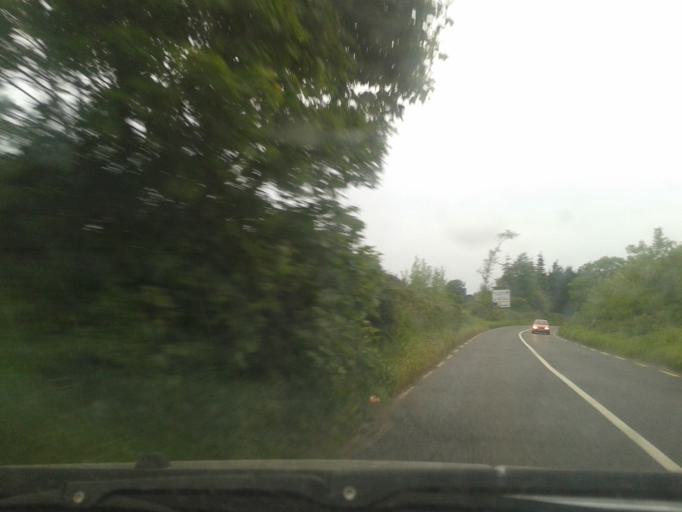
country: IE
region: Leinster
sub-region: Dublin City
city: Finglas
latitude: 53.4119
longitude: -6.3072
